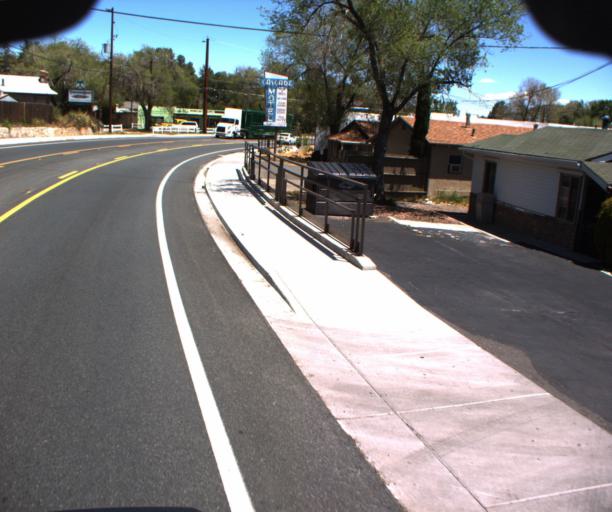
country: US
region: Arizona
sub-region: Yavapai County
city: Prescott
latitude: 34.5275
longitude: -112.4790
